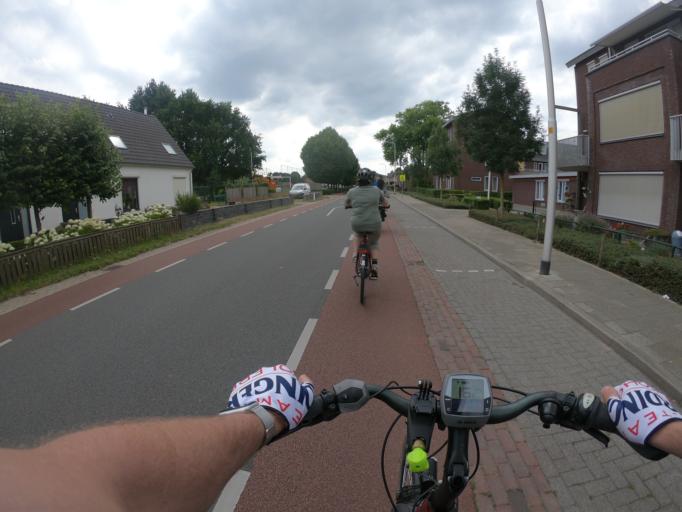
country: NL
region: Gelderland
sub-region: Gemeente Groesbeek
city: Bredeweg
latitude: 51.7568
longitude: 5.9407
